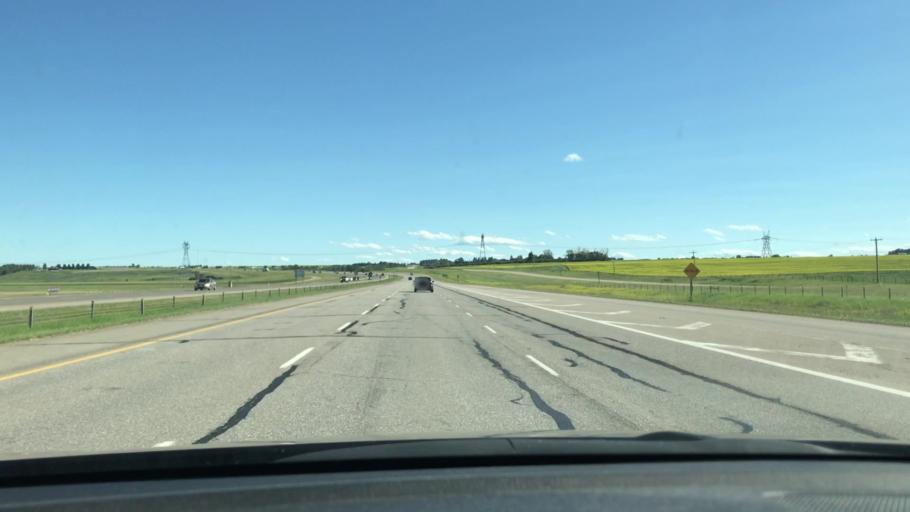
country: CA
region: Alberta
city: Crossfield
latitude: 51.4708
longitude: -114.0253
